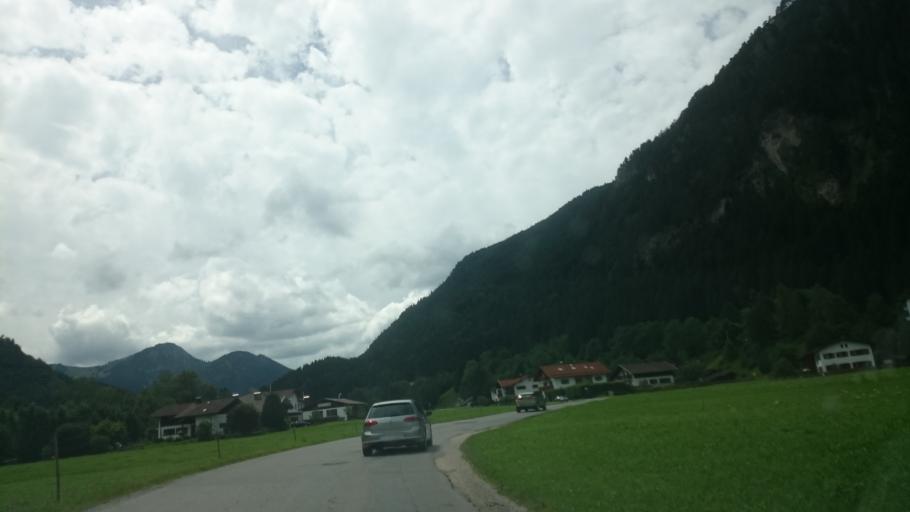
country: DE
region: Bavaria
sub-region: Swabia
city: Pfronten
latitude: 47.5689
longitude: 10.5539
